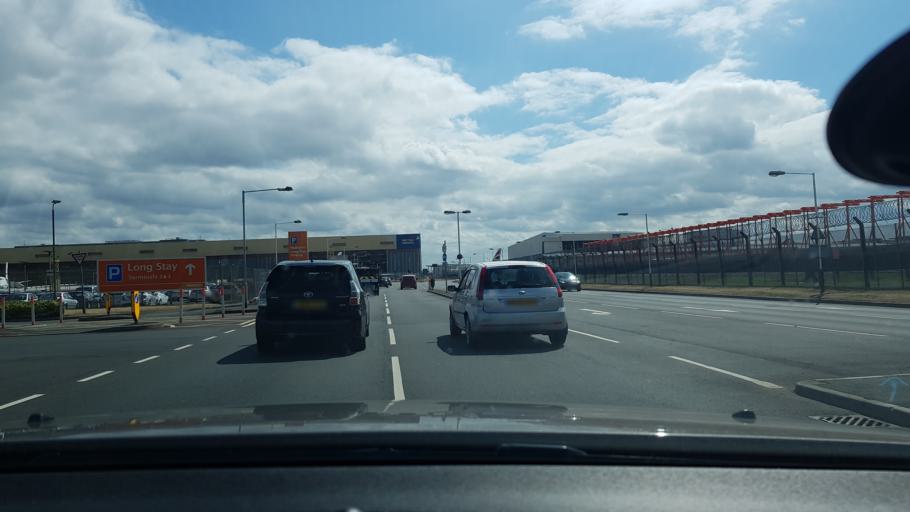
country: GB
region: England
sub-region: Greater London
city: Feltham
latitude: 51.4785
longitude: -0.4263
